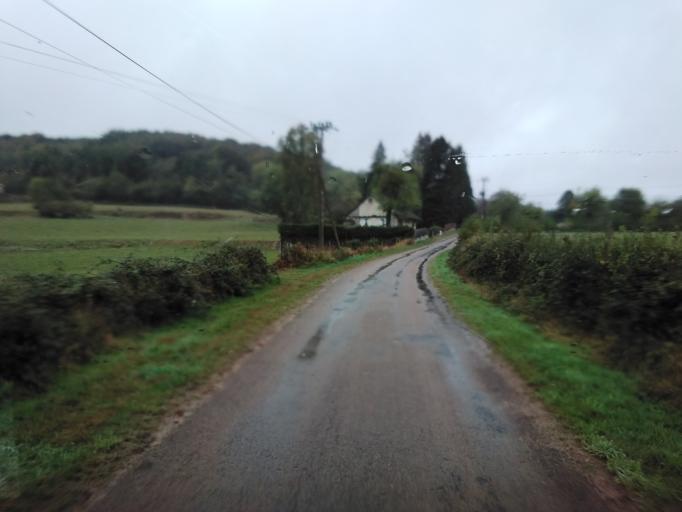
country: FR
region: Bourgogne
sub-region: Departement de la Nievre
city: Lormes
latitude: 47.2932
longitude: 3.9714
